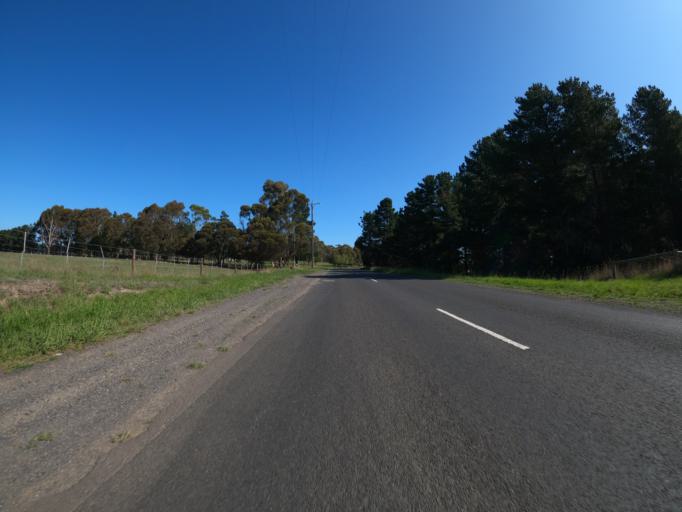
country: AU
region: Victoria
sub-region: Hume
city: Greenvale
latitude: -37.5486
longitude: 144.8688
